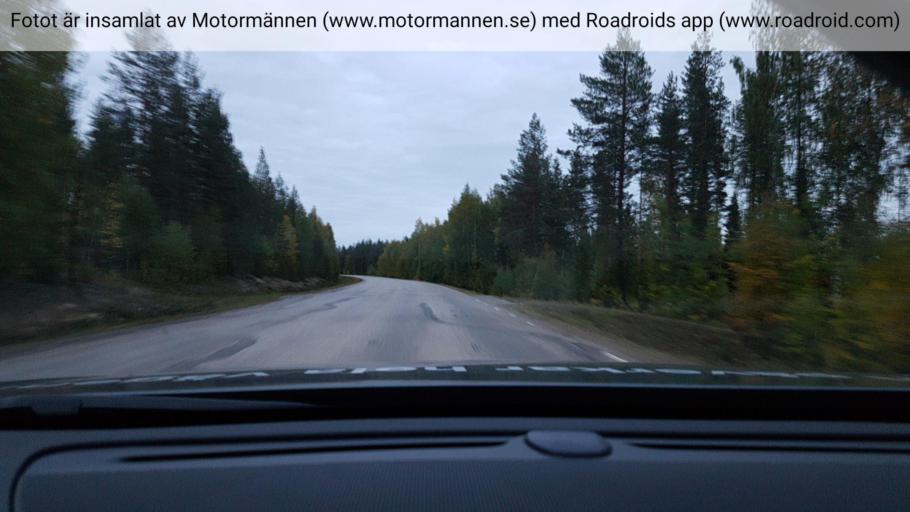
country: SE
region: Norrbotten
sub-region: Alvsbyns Kommun
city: AElvsbyn
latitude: 65.8487
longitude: 20.4588
